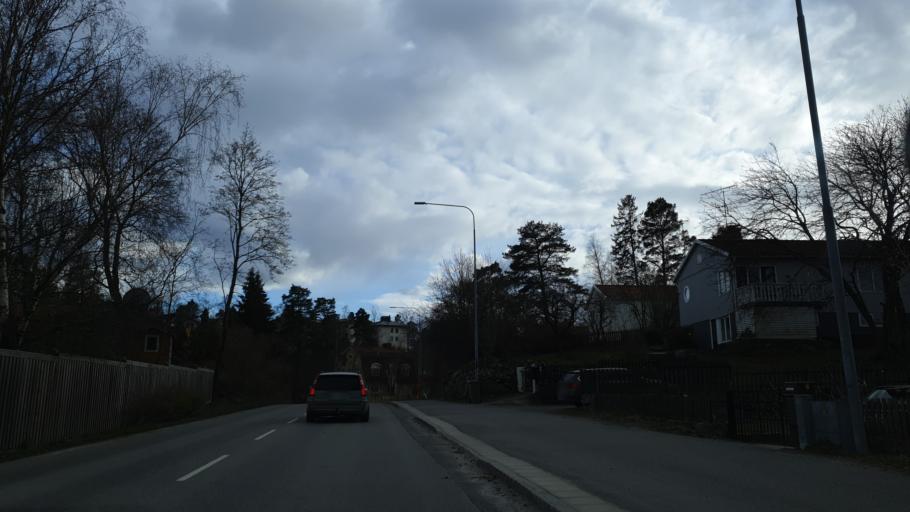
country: SE
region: Stockholm
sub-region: Lidingo
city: Lidingoe
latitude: 59.3720
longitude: 18.1326
